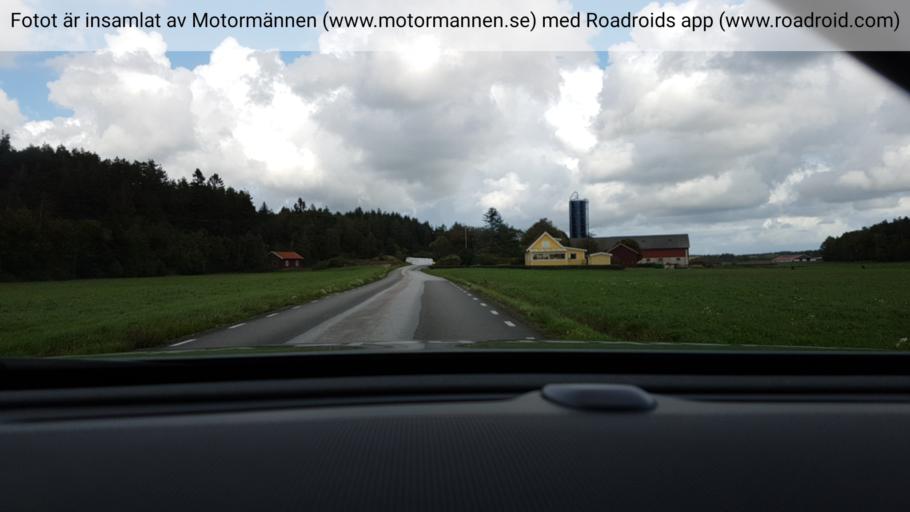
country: SE
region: Vaestra Goetaland
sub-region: Orust
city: Henan
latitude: 58.1440
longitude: 11.5736
